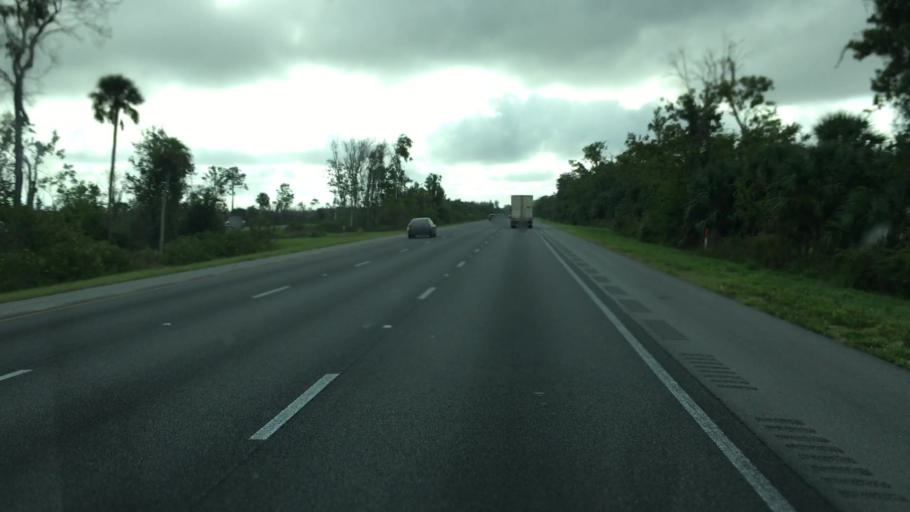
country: US
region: Florida
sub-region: Volusia County
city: Glencoe
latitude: 29.0373
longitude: -81.0043
